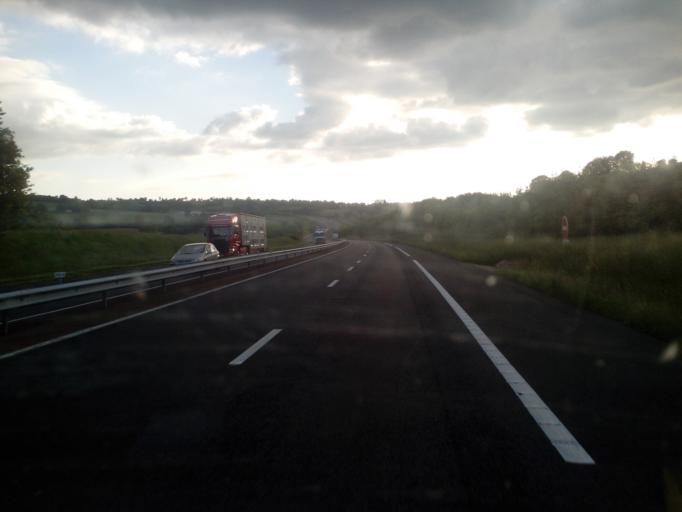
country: FR
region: Lower Normandy
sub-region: Departement de la Manche
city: Tessy-sur-Vire
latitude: 48.9406
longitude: -1.0539
